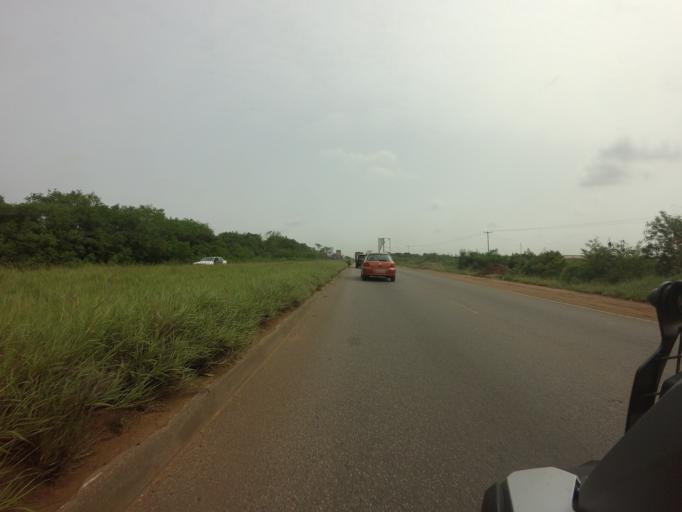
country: GH
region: Greater Accra
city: Tema
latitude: 5.7032
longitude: 0.0036
